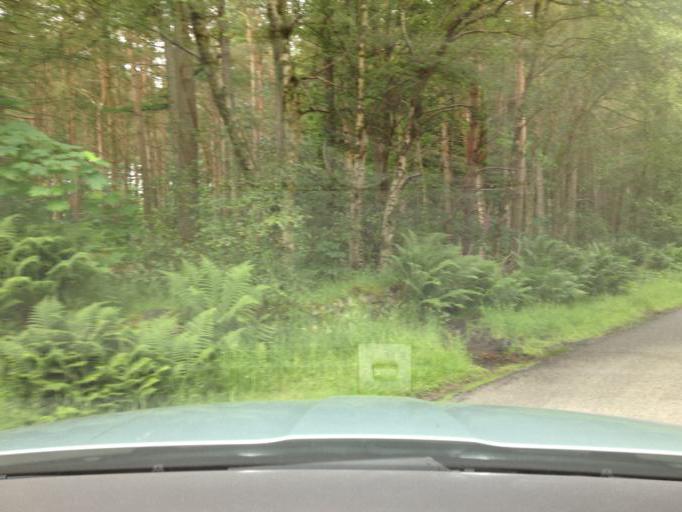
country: GB
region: Scotland
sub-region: Angus
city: Brechin
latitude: 56.8409
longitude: -2.6653
